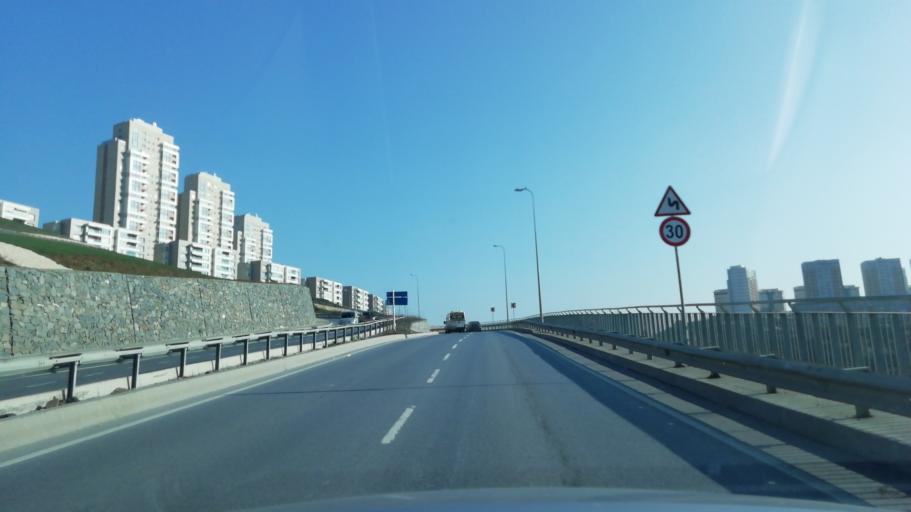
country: TR
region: Istanbul
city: Esenyurt
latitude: 41.0798
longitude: 28.6859
